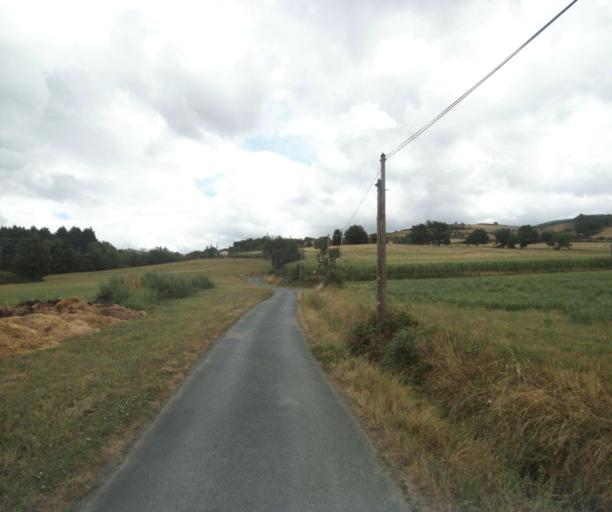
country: FR
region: Rhone-Alpes
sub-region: Departement du Rhone
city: Courzieu
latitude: 45.7479
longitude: 4.5469
